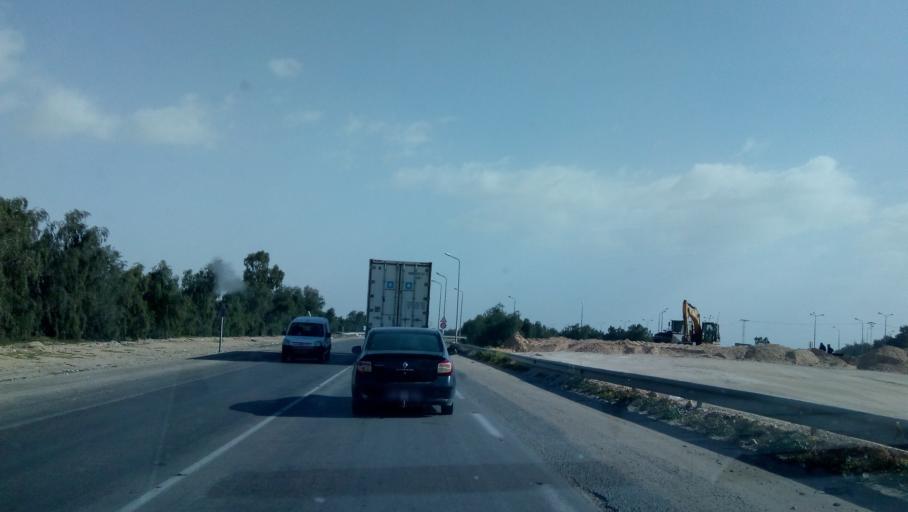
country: TN
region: Qabis
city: Gabes
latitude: 33.8871
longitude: 10.0194
